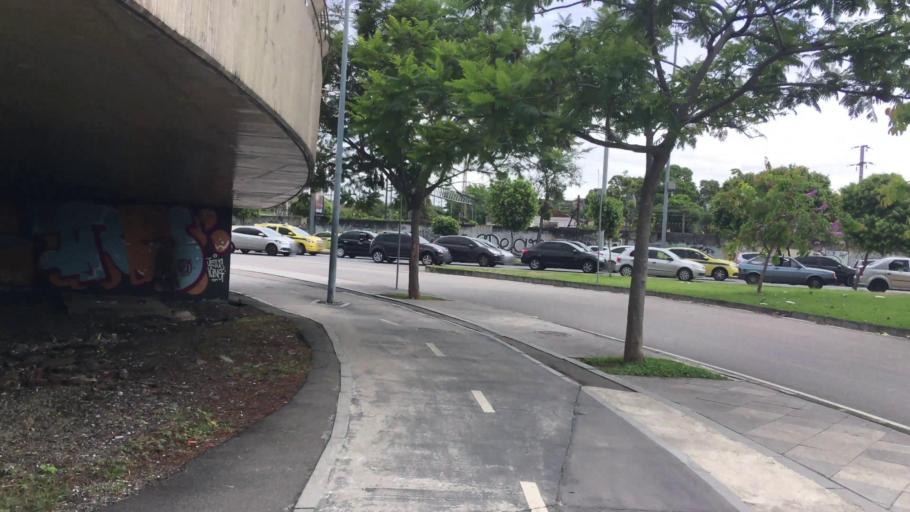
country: BR
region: Rio de Janeiro
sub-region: Rio De Janeiro
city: Rio de Janeiro
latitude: -22.9114
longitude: -43.2262
